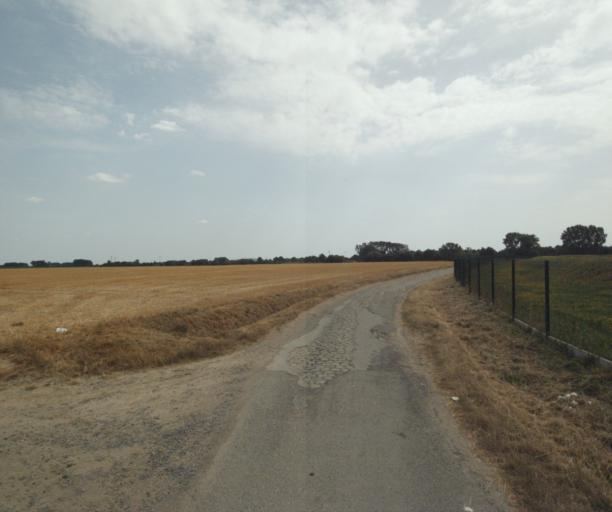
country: FR
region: Nord-Pas-de-Calais
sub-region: Departement du Nord
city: Leers
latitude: 50.6950
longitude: 3.2480
